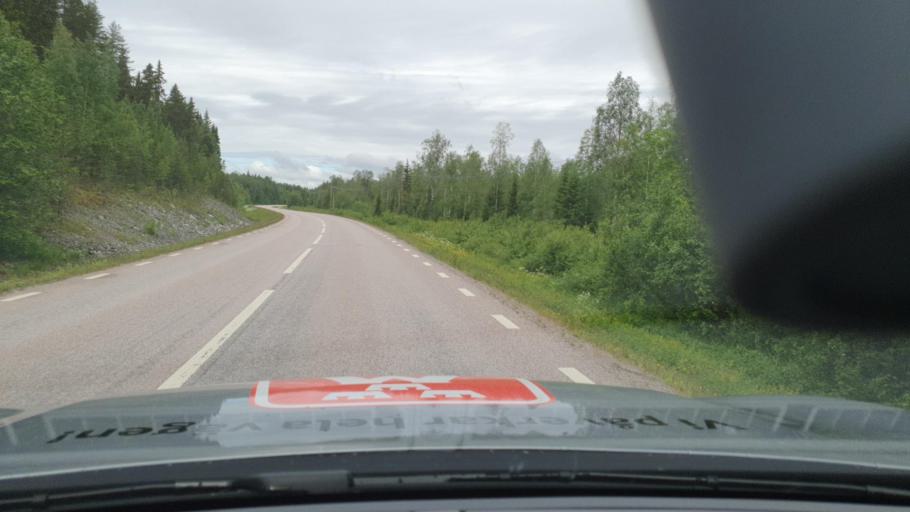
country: SE
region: Norrbotten
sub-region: Lulea Kommun
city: Ranea
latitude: 65.8719
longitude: 22.2959
